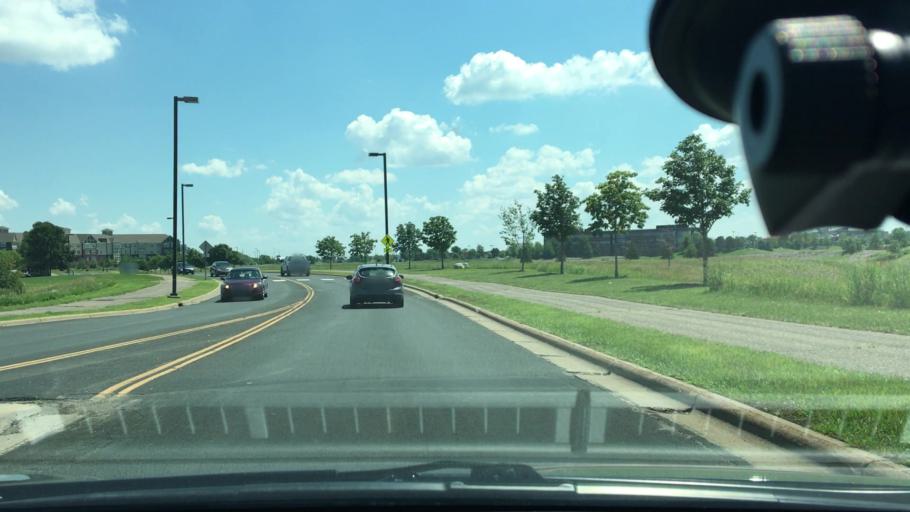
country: US
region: Minnesota
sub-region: Hennepin County
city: Maple Grove
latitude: 45.0983
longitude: -93.4394
